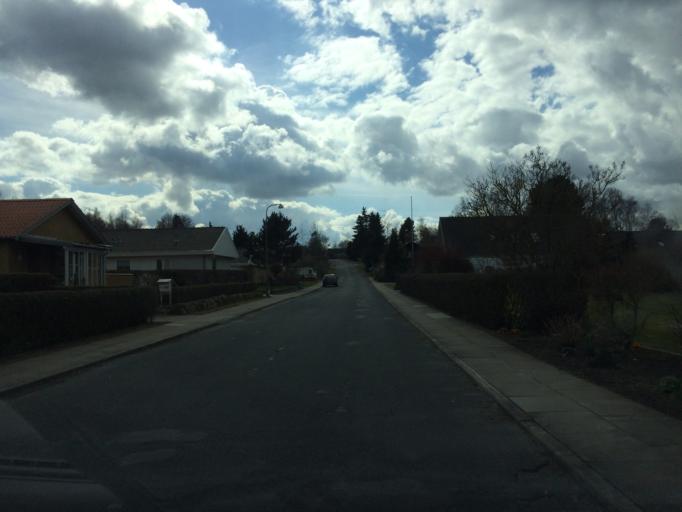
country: DK
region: South Denmark
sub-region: Nordfyns Kommune
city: Sonderso
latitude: 55.4161
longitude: 10.2748
